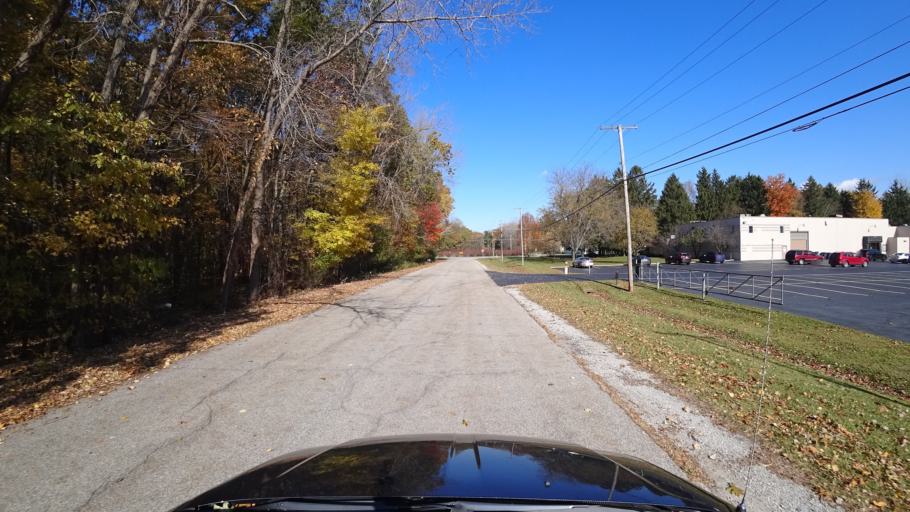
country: US
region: Indiana
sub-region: LaPorte County
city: Long Beach
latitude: 41.7372
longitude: -86.8310
